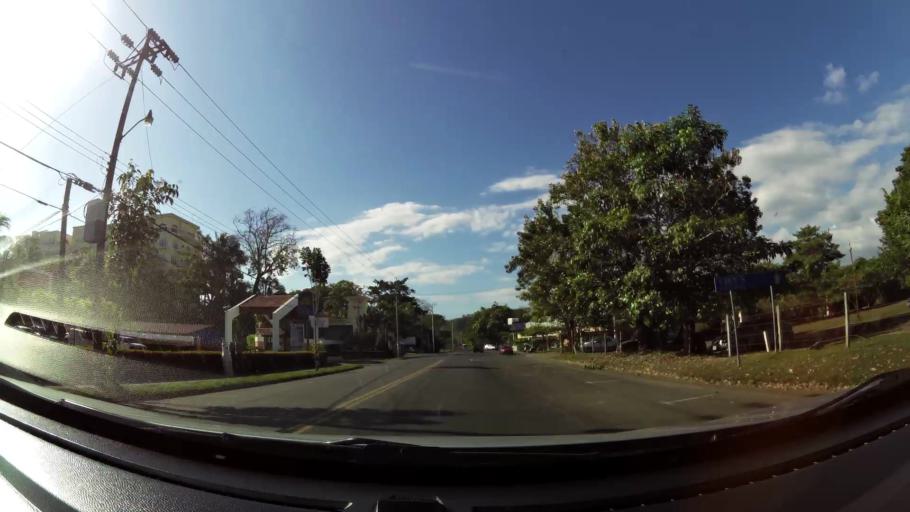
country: CR
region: Puntarenas
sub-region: Canton de Garabito
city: Jaco
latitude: 9.6202
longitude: -84.6348
